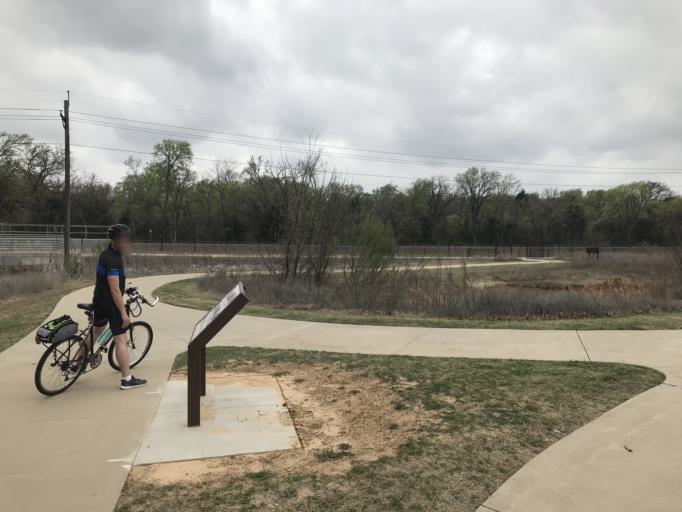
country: US
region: Texas
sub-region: Denton County
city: Corinth
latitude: 33.1668
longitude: -97.0731
